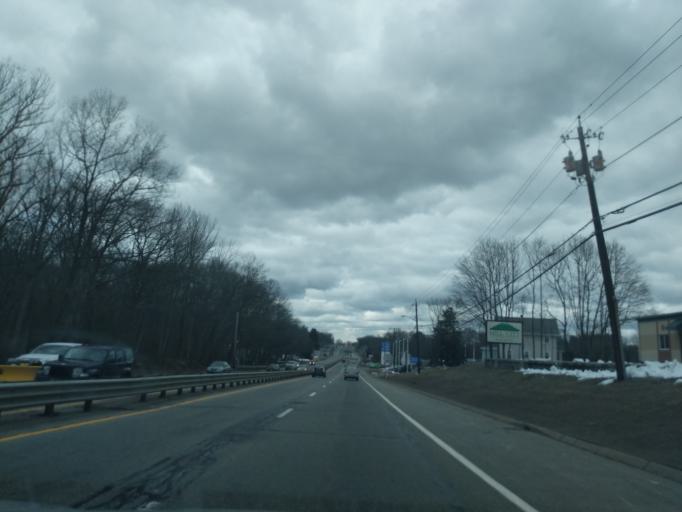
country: US
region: Rhode Island
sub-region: Providence County
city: Cumberland Hill
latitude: 41.9527
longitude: -71.4867
